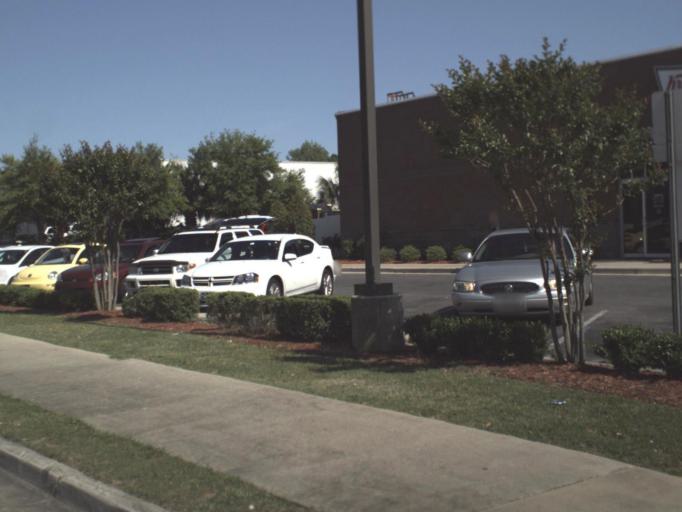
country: US
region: Florida
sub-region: Escambia County
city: Pensacola
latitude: 30.4231
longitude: -87.2068
